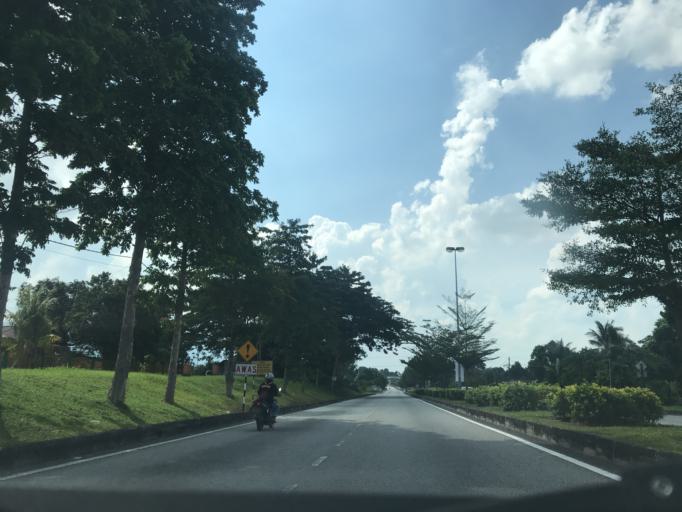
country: MY
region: Perak
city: Ipoh
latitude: 4.6325
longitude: 101.1146
